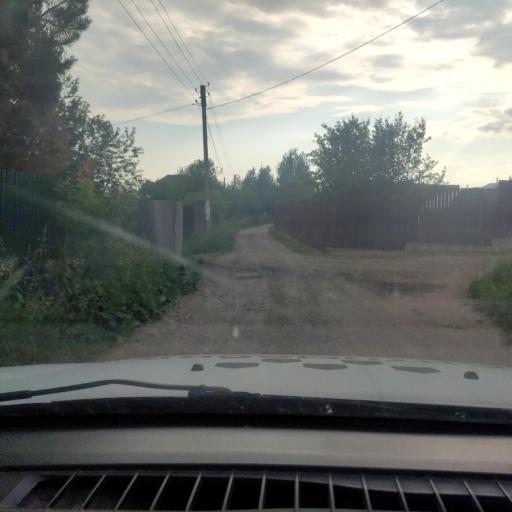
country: RU
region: Perm
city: Polazna
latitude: 58.1707
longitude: 56.3602
